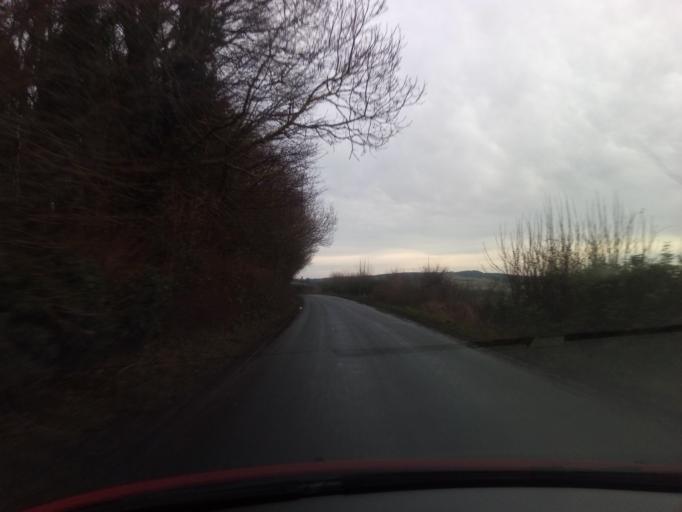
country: GB
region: England
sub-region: Northumberland
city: Whittingham
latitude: 55.4852
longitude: -1.8927
